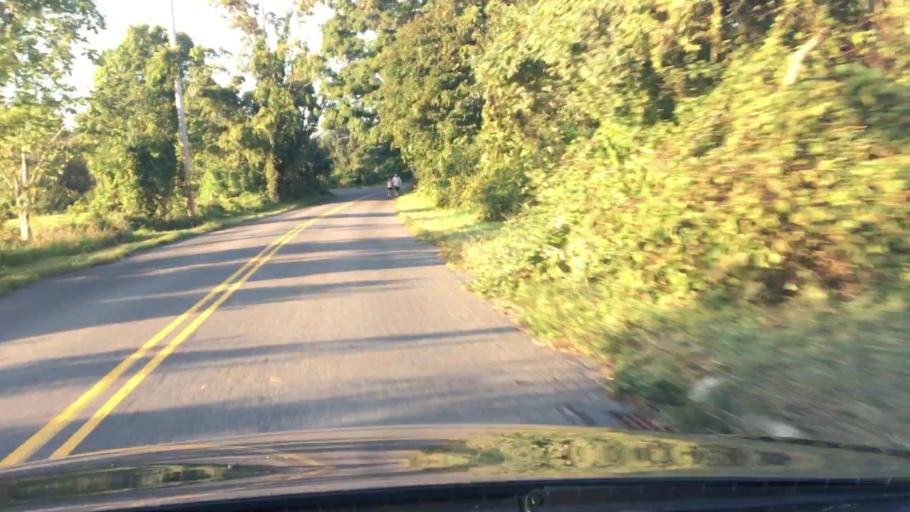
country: US
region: Connecticut
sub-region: Litchfield County
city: New Milford
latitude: 41.6078
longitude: -73.3732
